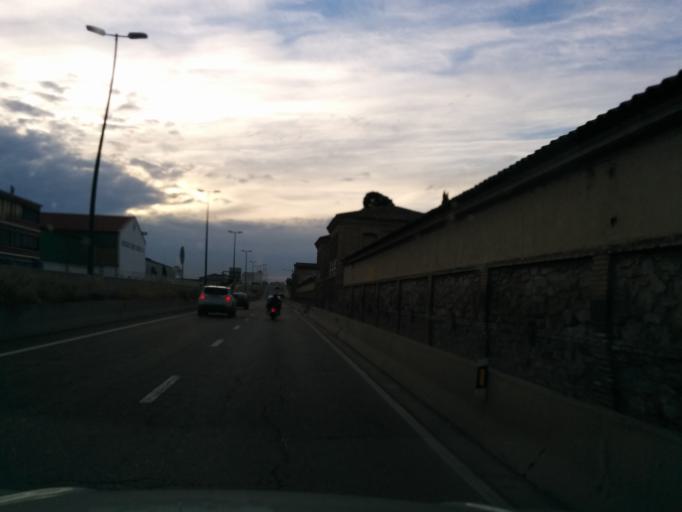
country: ES
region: Aragon
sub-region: Provincia de Zaragoza
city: Zaragoza
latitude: 41.6288
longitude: -0.8537
